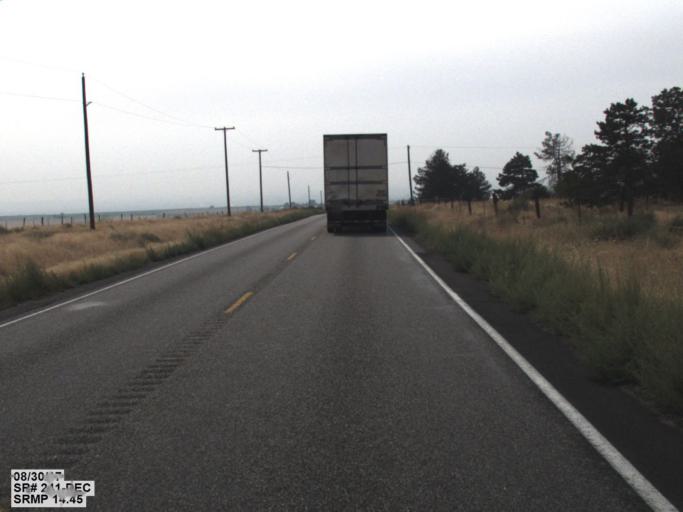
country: US
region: Washington
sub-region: Yakima County
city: Sunnyside
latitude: 46.4005
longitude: -119.9501
